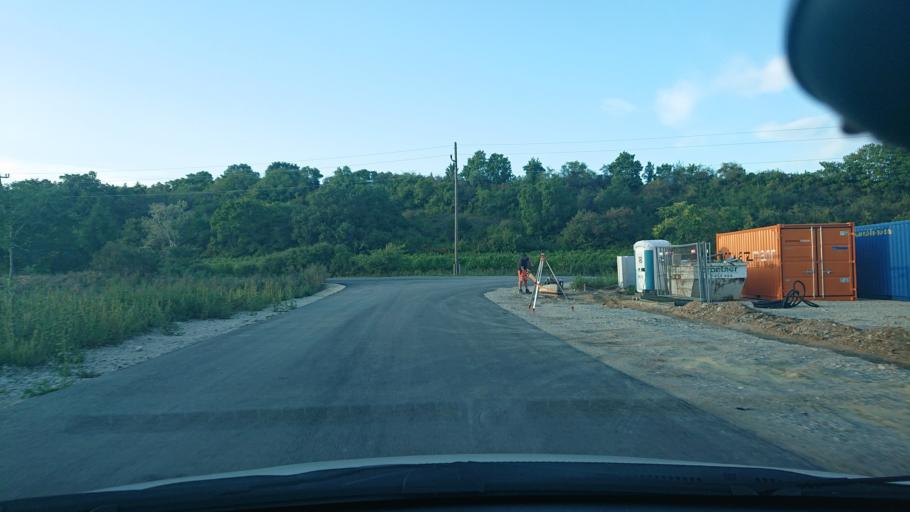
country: AT
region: Lower Austria
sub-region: Politischer Bezirk Baden
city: Leobersdorf
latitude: 47.9323
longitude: 16.2003
